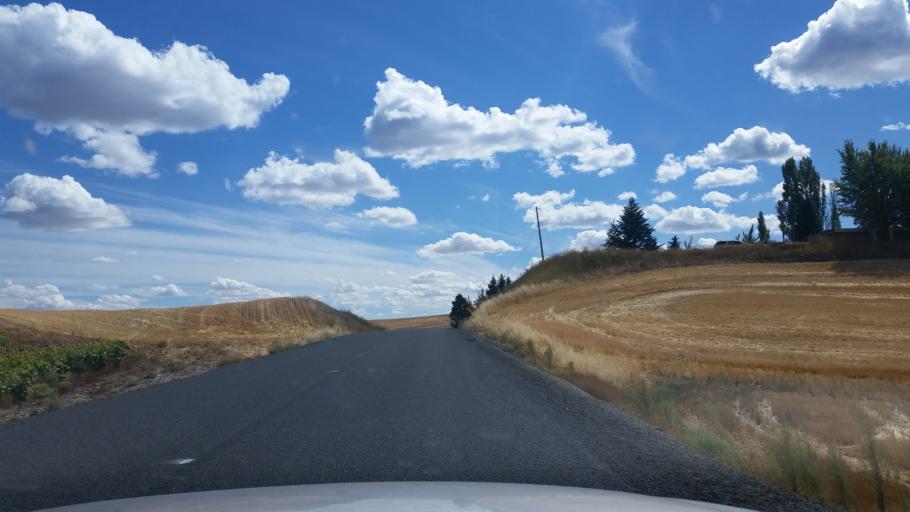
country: US
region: Washington
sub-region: Spokane County
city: Cheney
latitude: 47.4862
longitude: -117.6157
